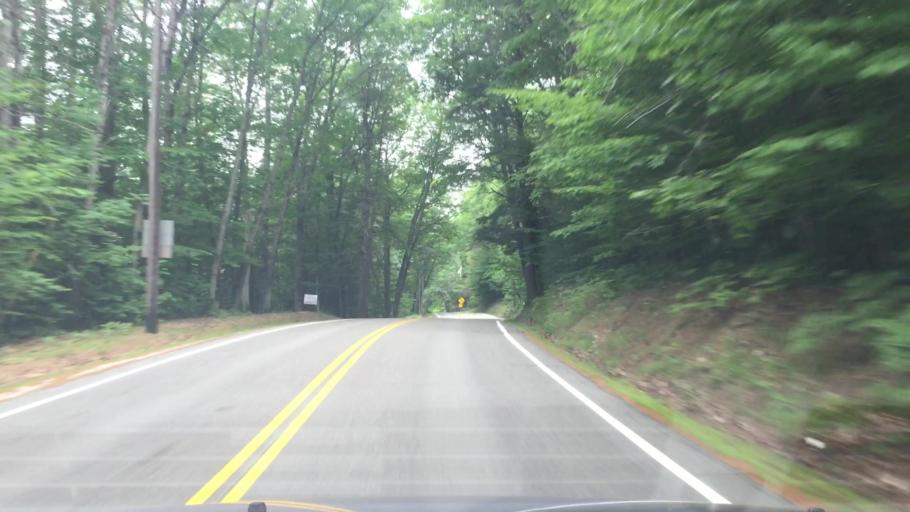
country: US
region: New Hampshire
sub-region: Carroll County
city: Madison
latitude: 43.8889
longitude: -71.0728
